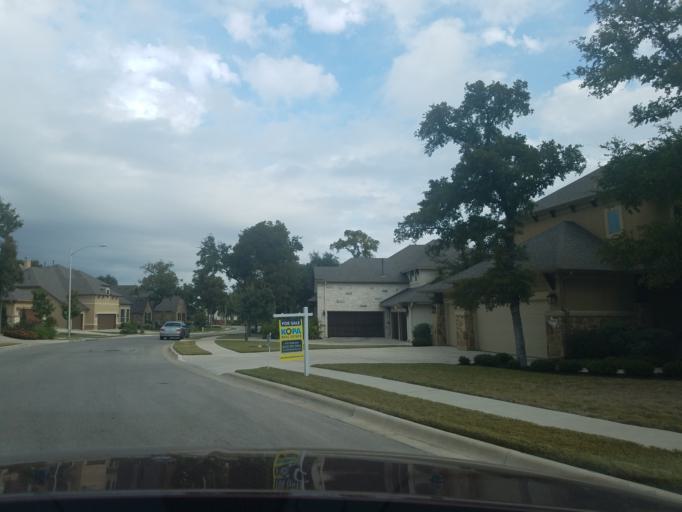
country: US
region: Texas
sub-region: Williamson County
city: Anderson Mill
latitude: 30.4850
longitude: -97.7952
